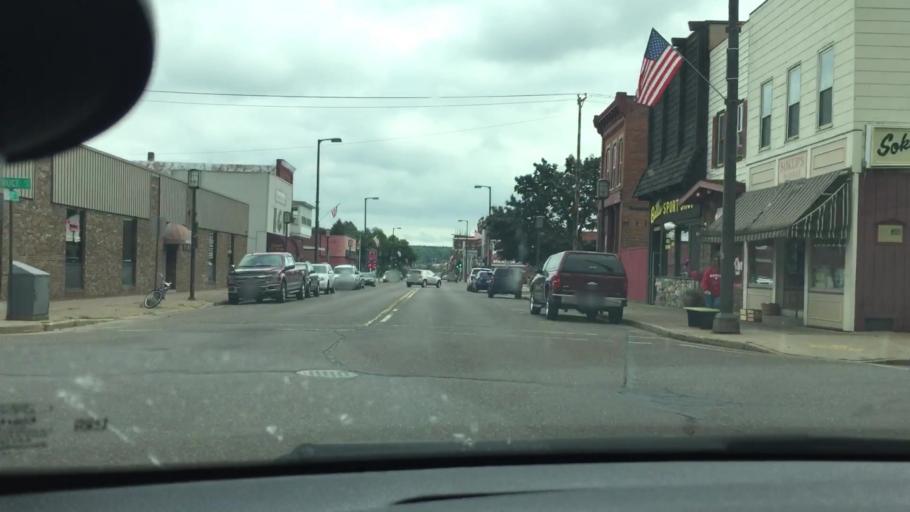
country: US
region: Wisconsin
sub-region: Chippewa County
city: Chippewa Falls
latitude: 44.9398
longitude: -91.3966
